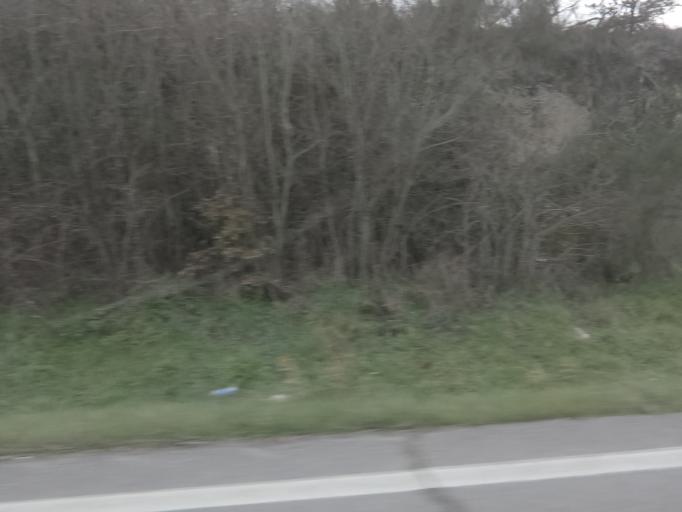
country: ES
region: Galicia
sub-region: Provincia de Ourense
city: Allariz
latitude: 42.1991
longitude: -7.8036
